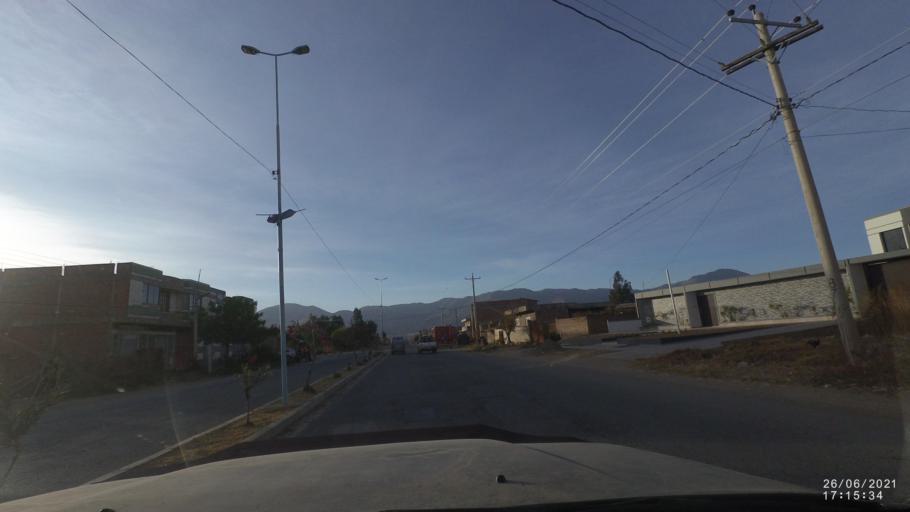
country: BO
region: Cochabamba
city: Cliza
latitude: -17.5705
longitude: -65.9351
